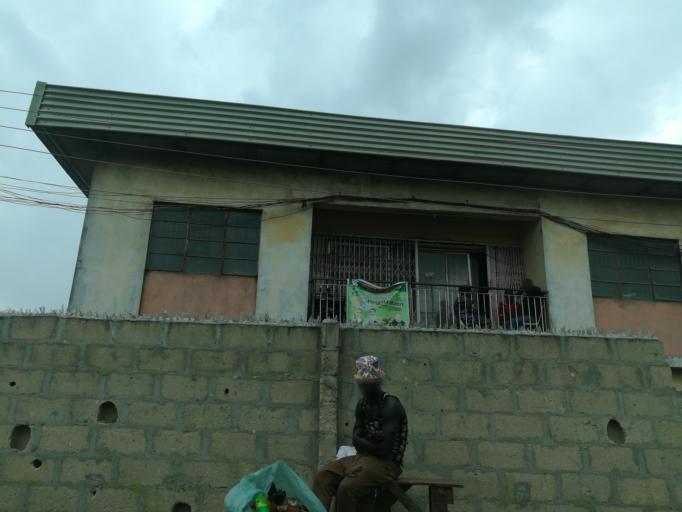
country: NG
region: Lagos
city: Ojota
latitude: 6.6113
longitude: 3.3974
